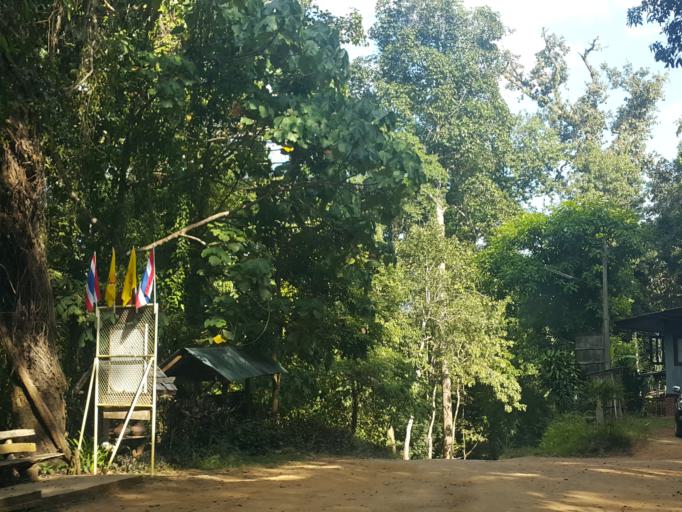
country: TH
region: Chiang Mai
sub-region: Amphoe Chiang Dao
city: Chiang Dao
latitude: 19.4033
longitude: 98.9220
